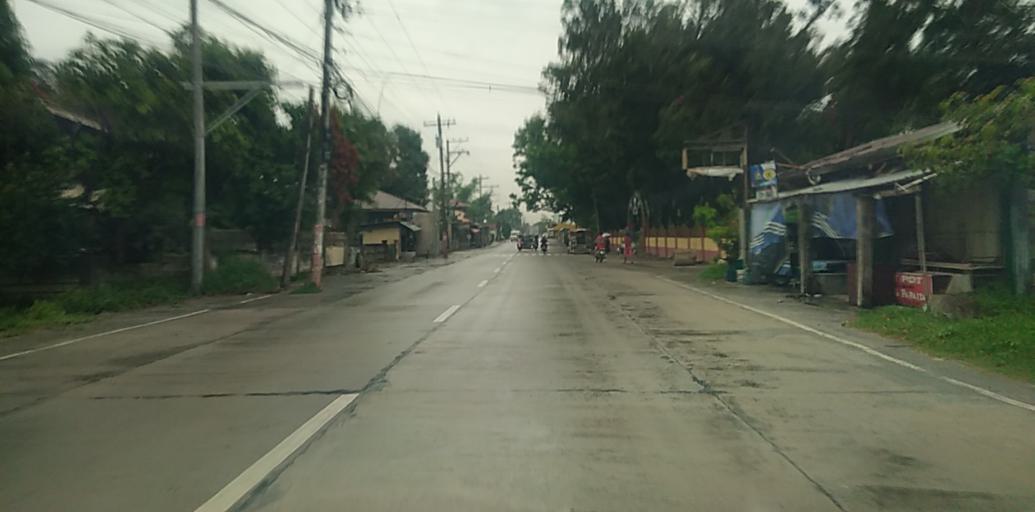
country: PH
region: Central Luzon
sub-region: Province of Pampanga
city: Anao
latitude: 15.1397
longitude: 120.6937
